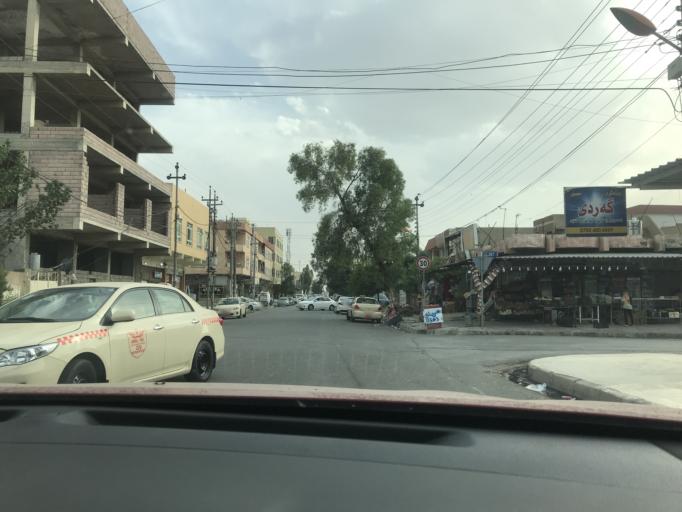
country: IQ
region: Arbil
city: Erbil
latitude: 36.1772
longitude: 43.9754
